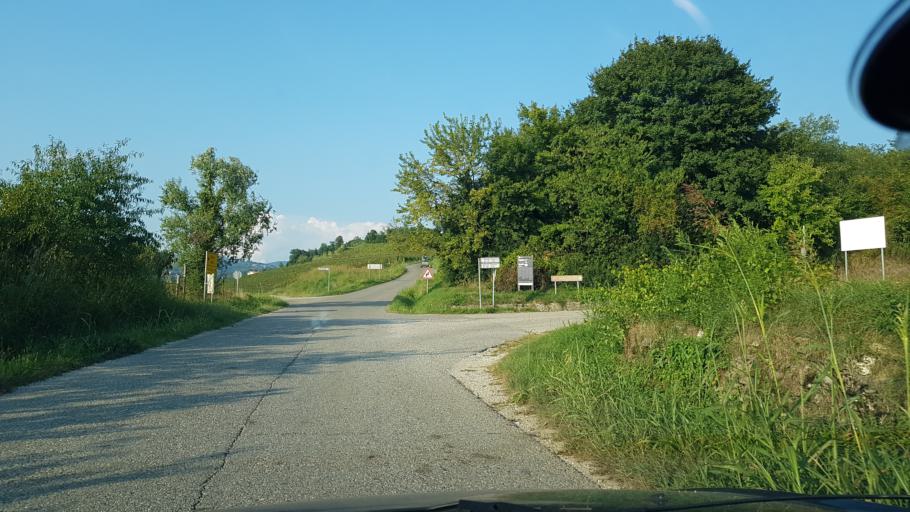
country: SI
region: Brda
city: Dobrovo
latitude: 45.9715
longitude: 13.5481
